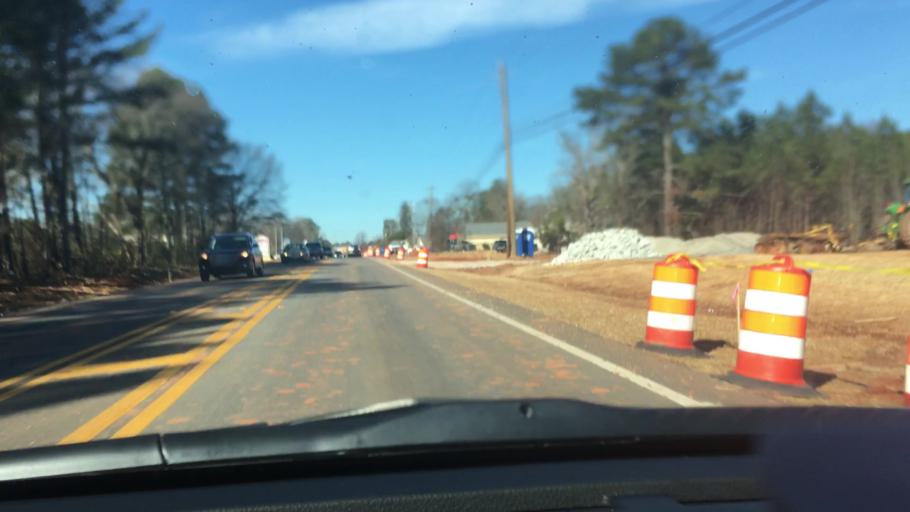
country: US
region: Georgia
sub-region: Henry County
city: McDonough
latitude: 33.4444
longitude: -84.1317
